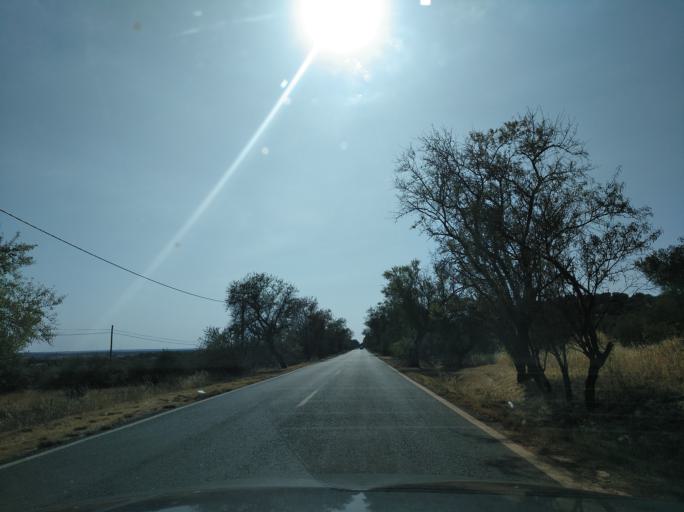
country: ES
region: Andalusia
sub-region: Provincia de Huelva
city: Rosal de la Frontera
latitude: 37.9535
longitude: -7.2826
